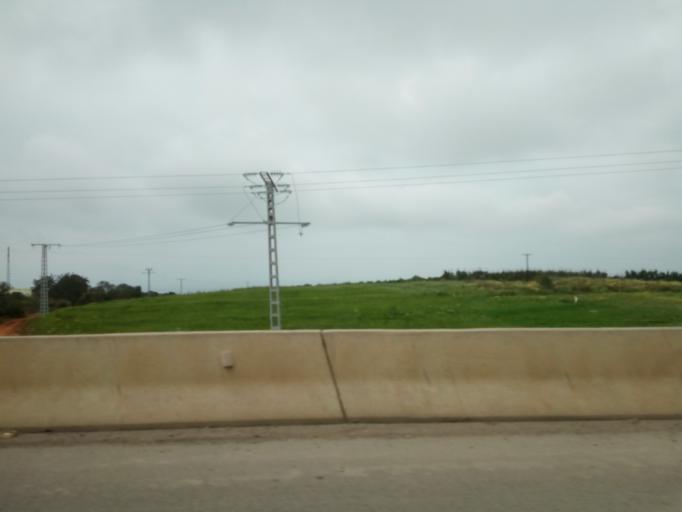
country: DZ
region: Tipaza
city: Bou Ismail
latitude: 36.6038
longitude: 2.6572
